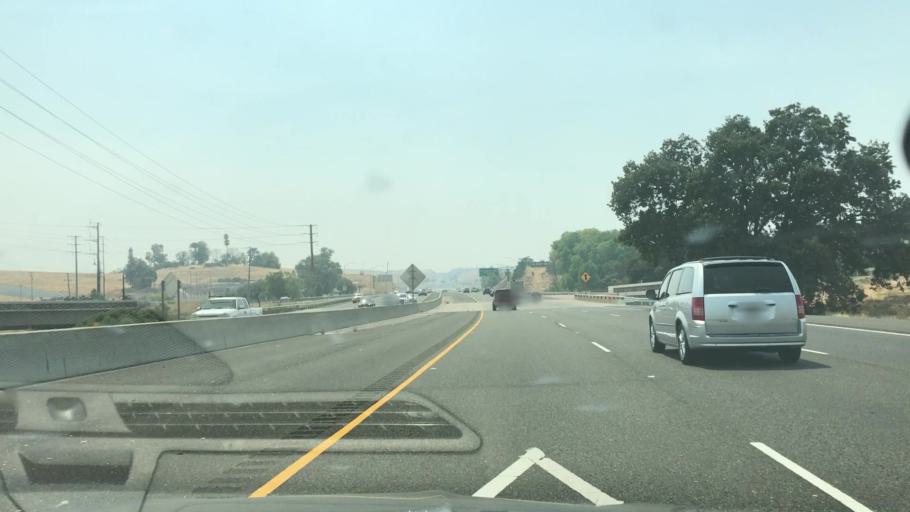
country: US
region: California
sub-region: El Dorado County
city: El Dorado Hills
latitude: 38.6580
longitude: -121.0560
